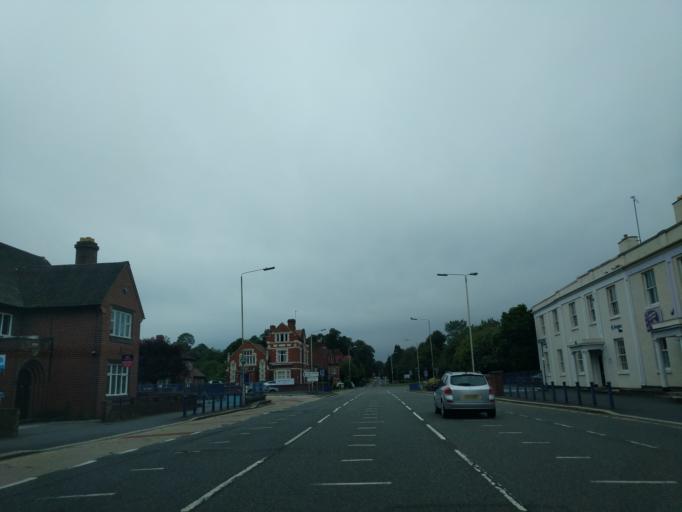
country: GB
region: England
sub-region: Dudley
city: Stourbridge
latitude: 52.4546
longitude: -2.1468
